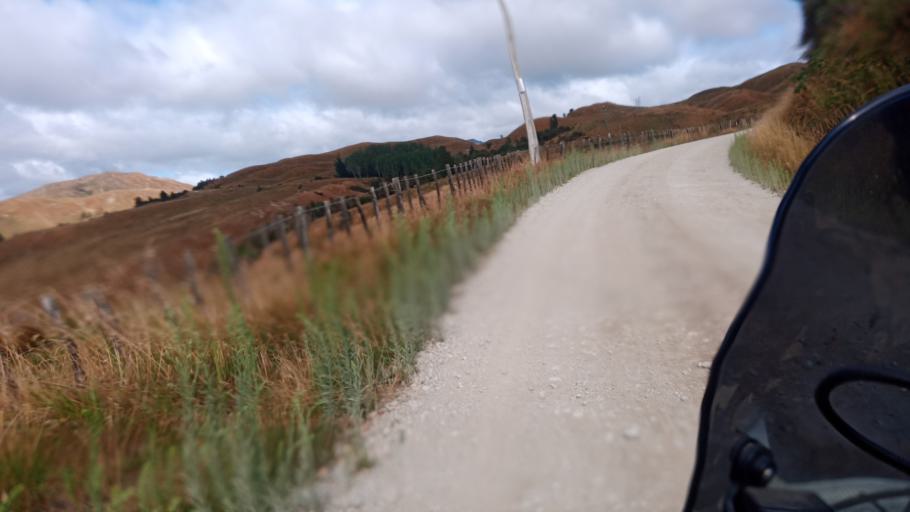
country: NZ
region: Hawke's Bay
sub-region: Wairoa District
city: Wairoa
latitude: -38.6040
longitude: 177.4723
